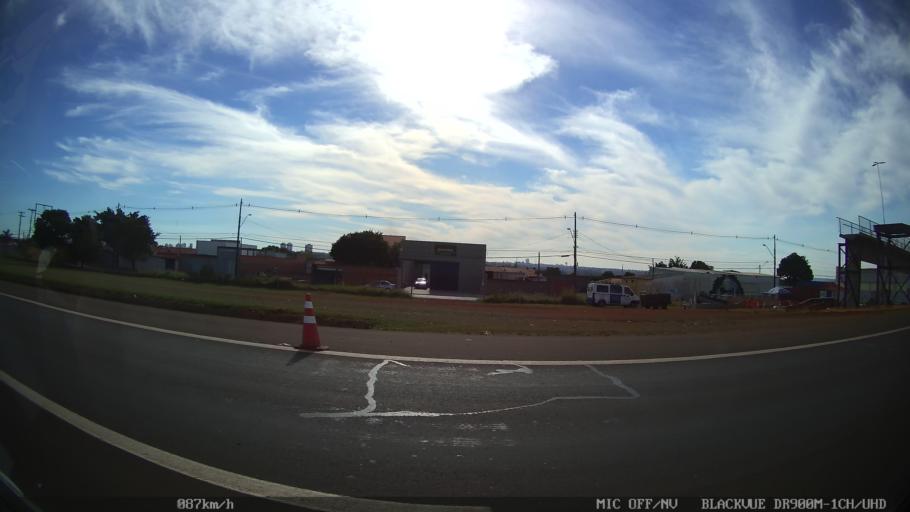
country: BR
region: Sao Paulo
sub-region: Araraquara
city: Araraquara
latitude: -21.8014
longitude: -48.1457
